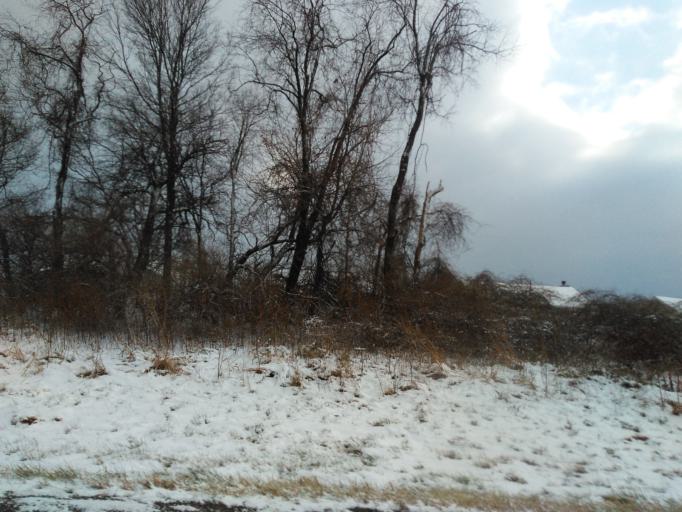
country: US
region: Illinois
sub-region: Madison County
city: Maryville
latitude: 38.7037
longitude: -89.9790
